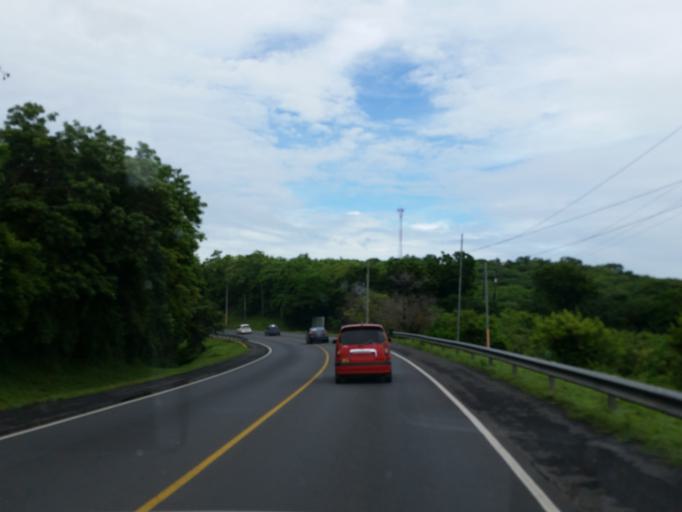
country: NI
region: Leon
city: Nagarote
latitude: 12.2440
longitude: -86.4425
